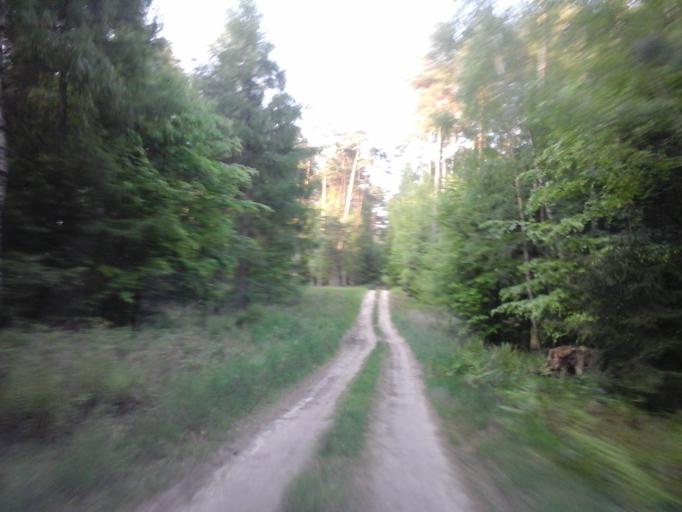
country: PL
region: West Pomeranian Voivodeship
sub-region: Powiat choszczenski
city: Krzecin
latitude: 53.0098
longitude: 15.5403
